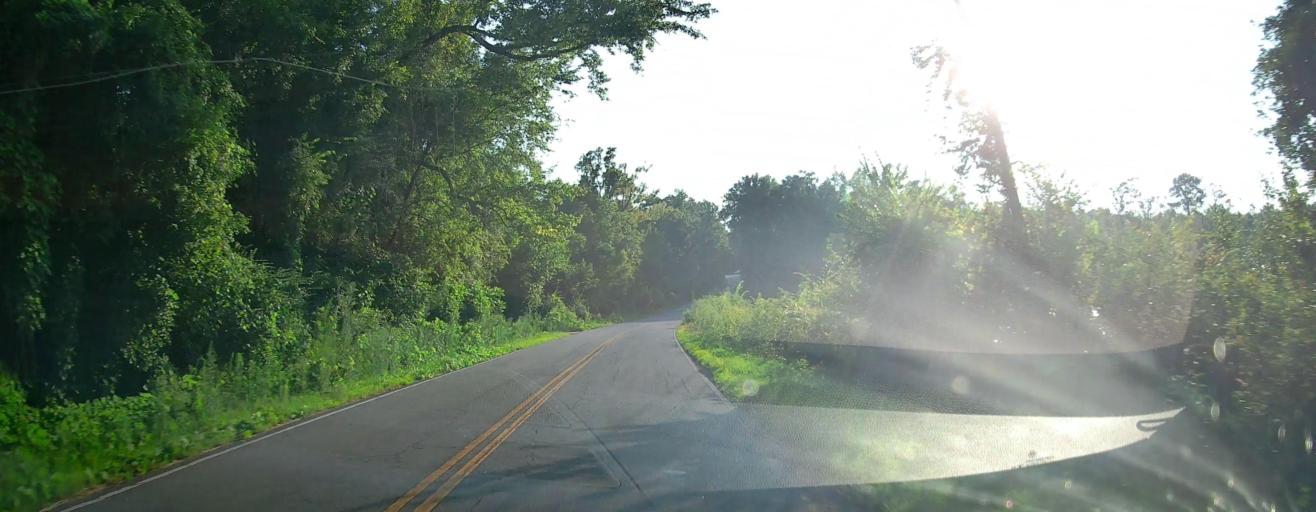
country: US
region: Georgia
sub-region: Peach County
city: Byron
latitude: 32.7258
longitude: -83.7537
